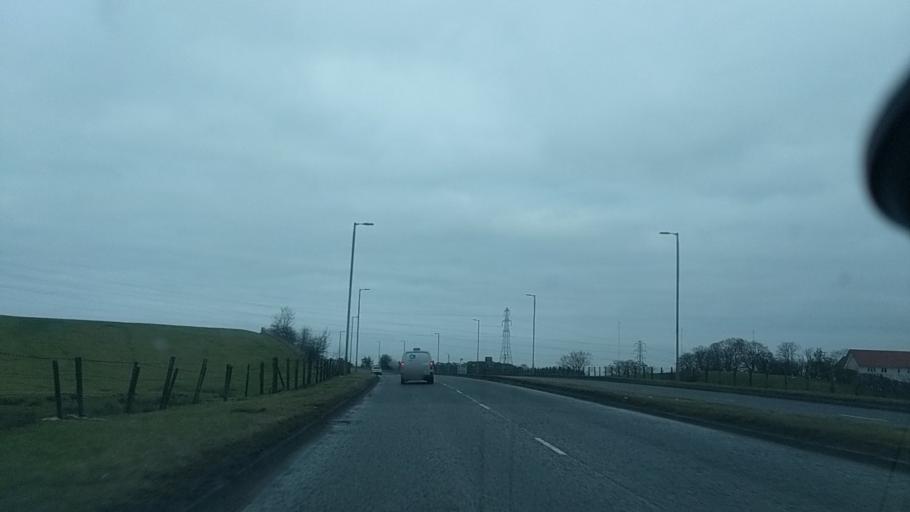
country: GB
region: Scotland
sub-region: South Lanarkshire
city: East Kilbride
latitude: 55.7880
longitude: -4.1665
